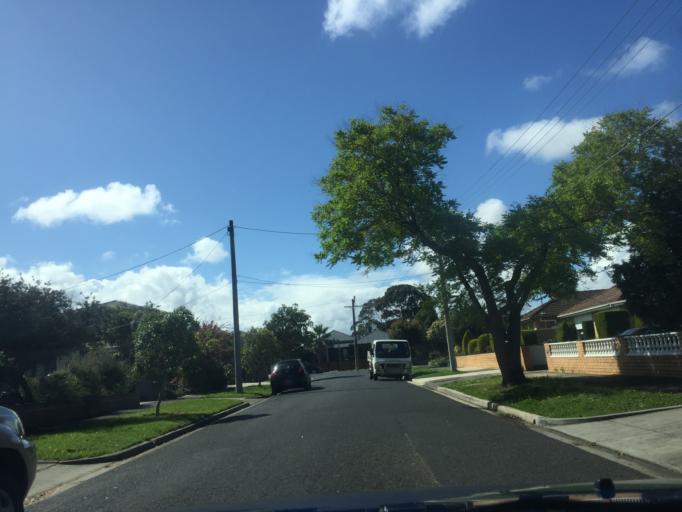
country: AU
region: Victoria
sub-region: Banyule
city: Bellfield
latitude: -37.7622
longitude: 145.0314
